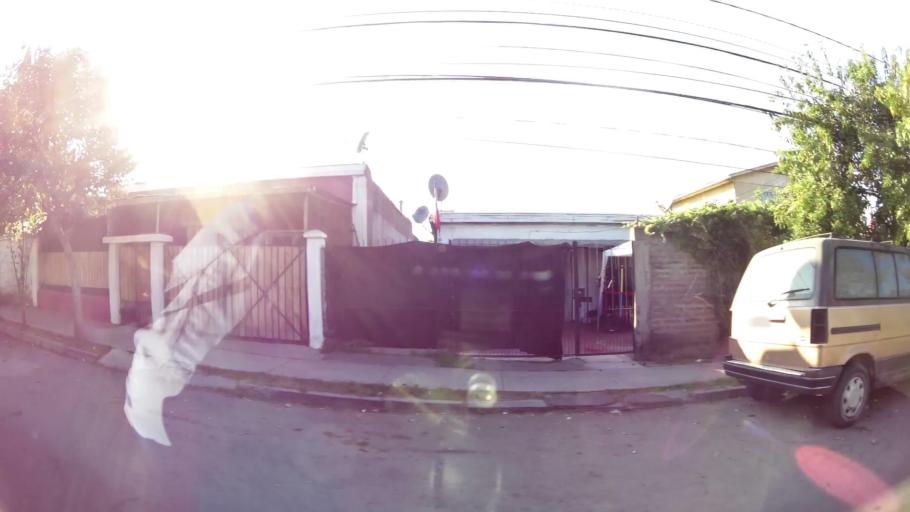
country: CL
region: Santiago Metropolitan
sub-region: Provincia de Santiago
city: Santiago
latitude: -33.3736
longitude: -70.6455
